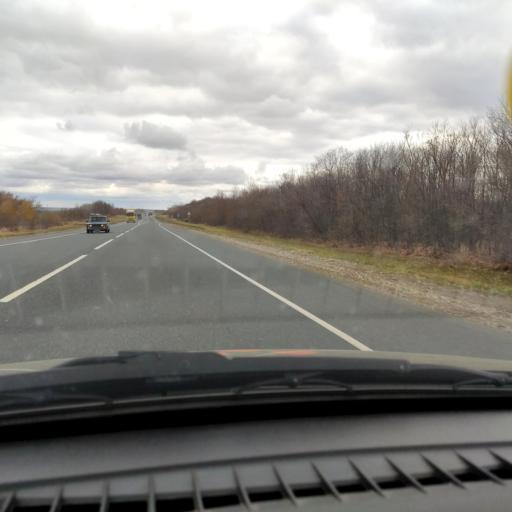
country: RU
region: Samara
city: Mezhdurechensk
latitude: 53.2589
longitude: 49.0928
